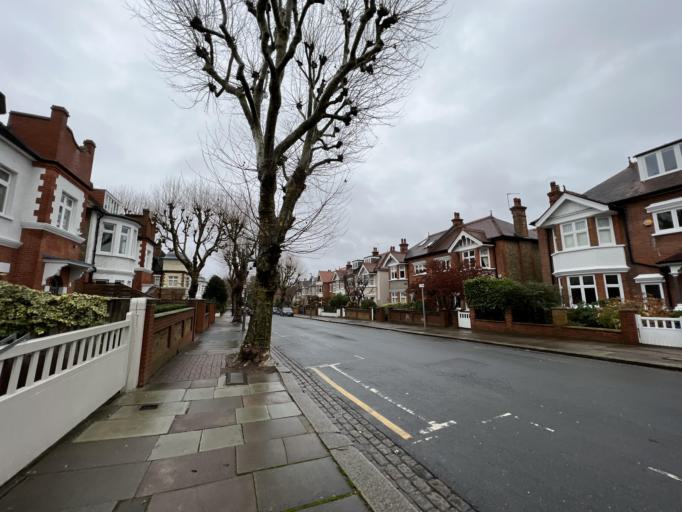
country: GB
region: England
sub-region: Greater London
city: Wandsworth
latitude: 51.4596
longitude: -0.2300
